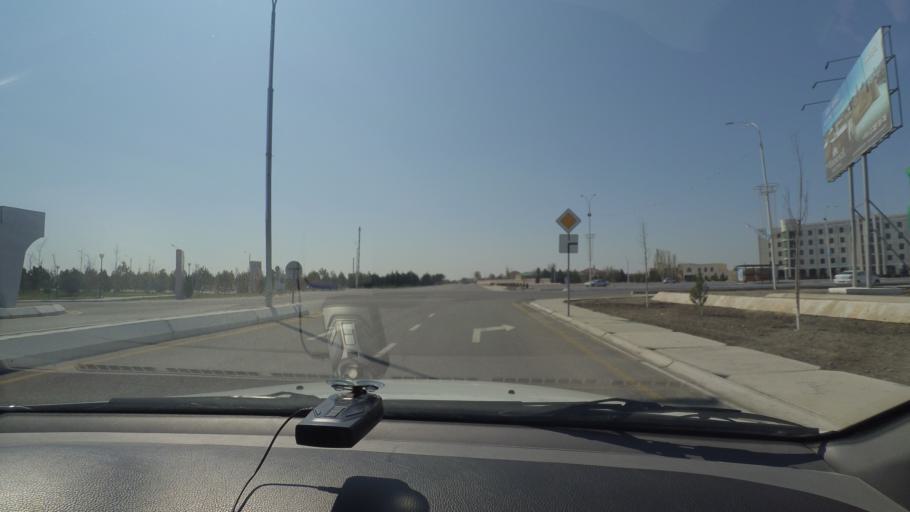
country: UZ
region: Bukhara
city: Bukhara
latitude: 39.7674
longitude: 64.4730
